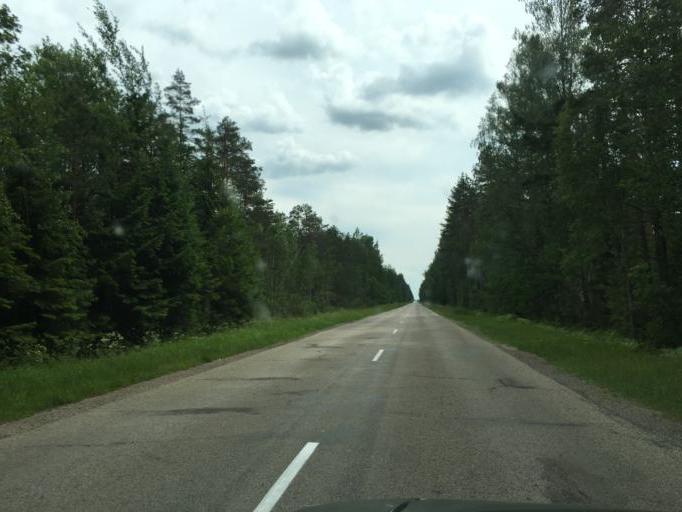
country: LV
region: Rugaju
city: Rugaji
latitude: 56.7896
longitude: 27.1014
